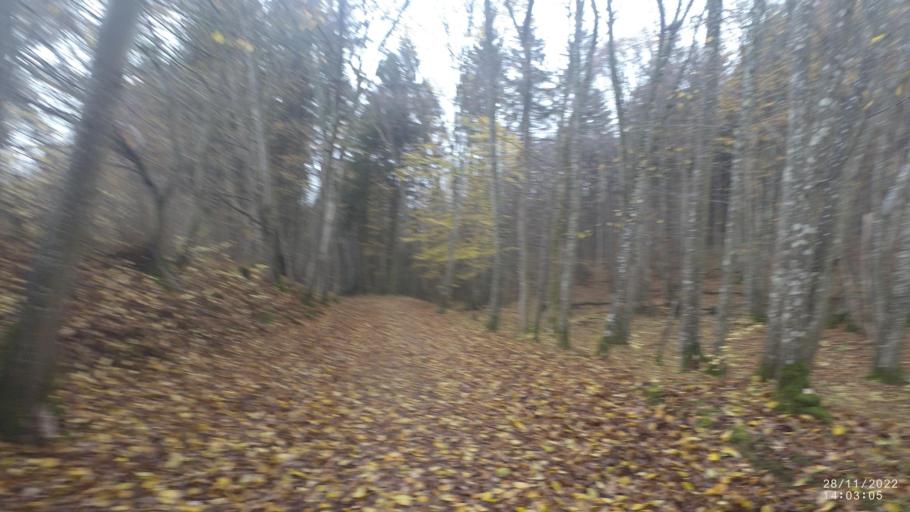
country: DE
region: Rheinland-Pfalz
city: Nohn
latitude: 50.3350
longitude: 6.7746
